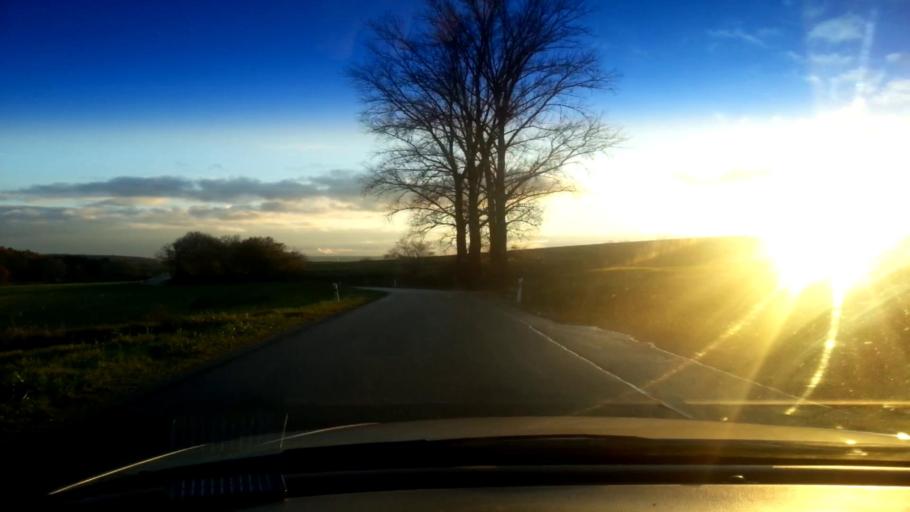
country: DE
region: Bavaria
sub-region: Upper Franconia
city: Buttenheim
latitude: 49.8254
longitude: 11.0566
